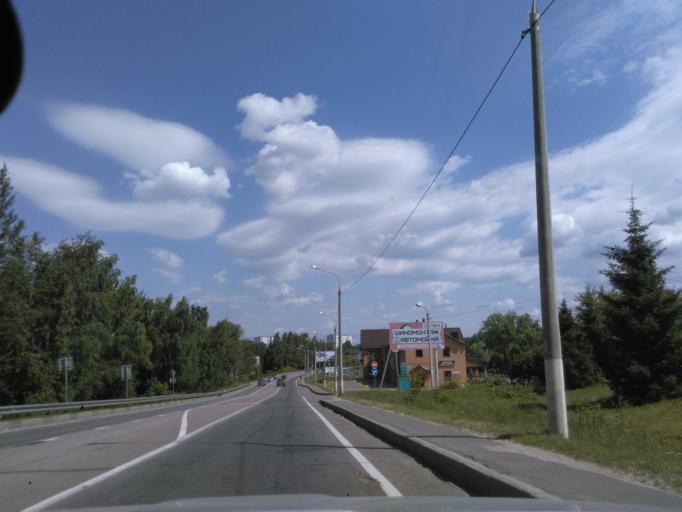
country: RU
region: Moskovskaya
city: Solnechnogorsk
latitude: 56.1847
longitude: 36.9614
